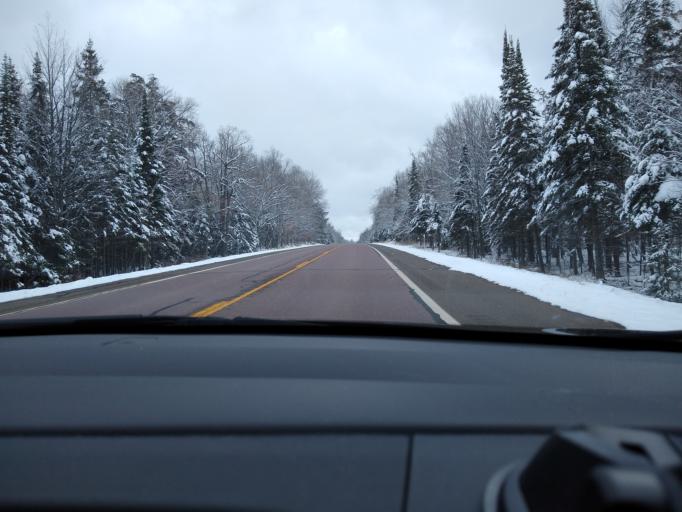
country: US
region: Michigan
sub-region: Iron County
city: Iron River
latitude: 46.1854
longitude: -88.9755
